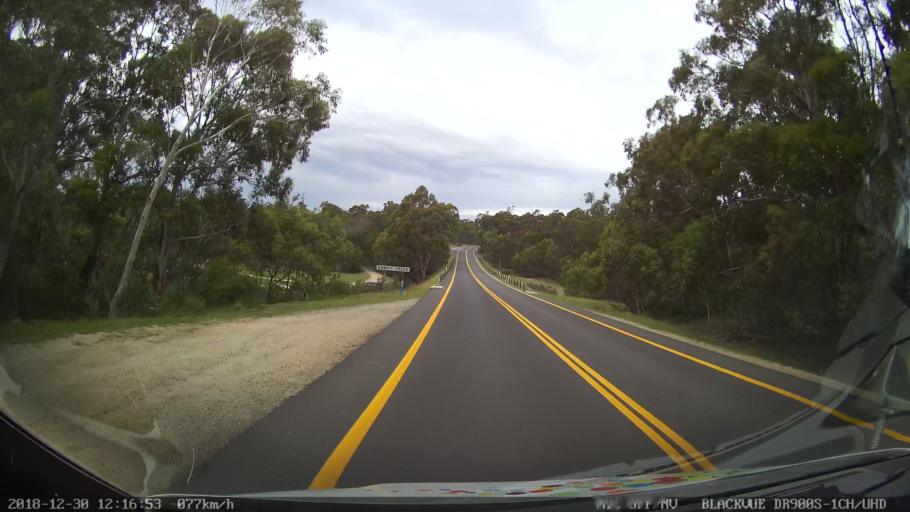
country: AU
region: New South Wales
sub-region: Snowy River
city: Jindabyne
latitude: -36.3492
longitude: 148.5634
